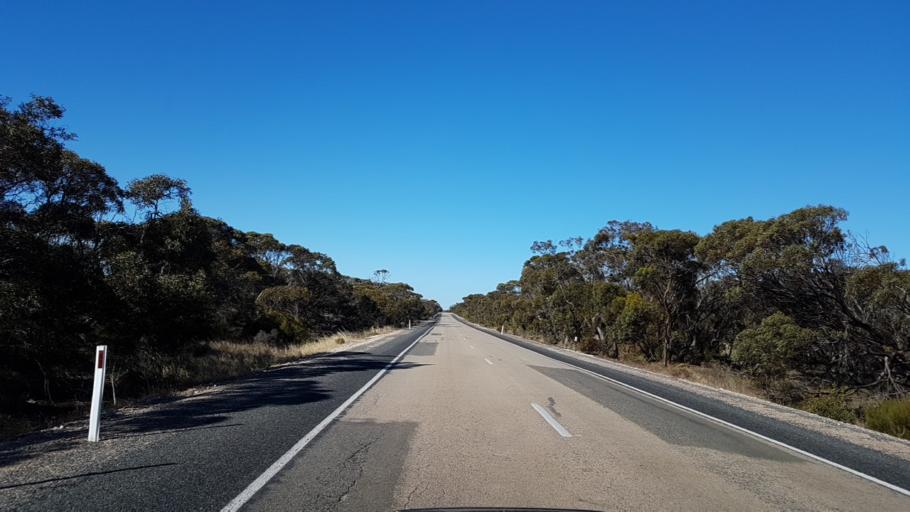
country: AU
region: South Australia
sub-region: Yorke Peninsula
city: Ardrossan
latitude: -34.6077
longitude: 137.7924
